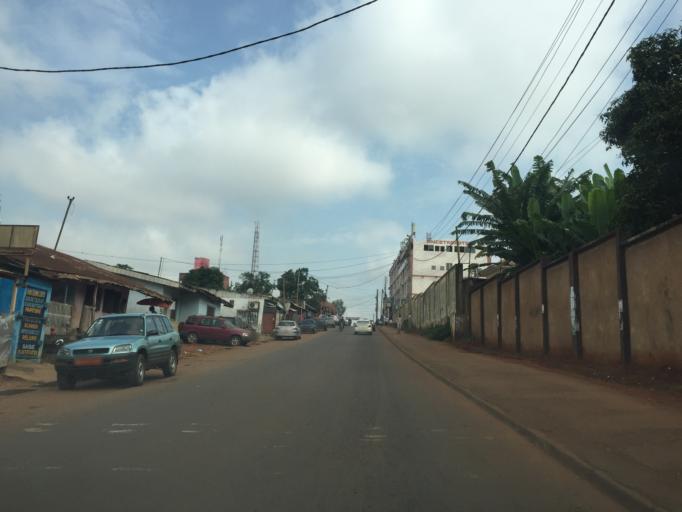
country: CM
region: Centre
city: Yaounde
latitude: 3.8557
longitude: 11.5054
